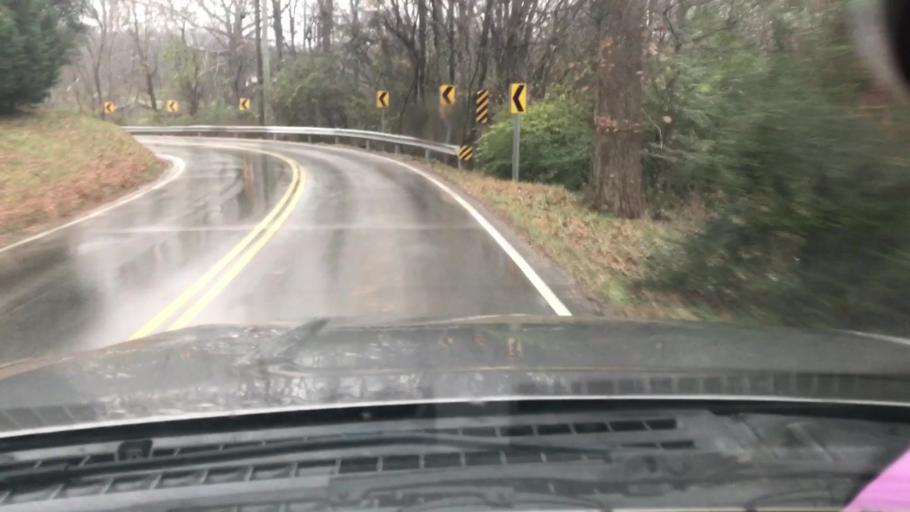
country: US
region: Tennessee
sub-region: Williamson County
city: Brentwood Estates
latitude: 36.0135
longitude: -86.7384
